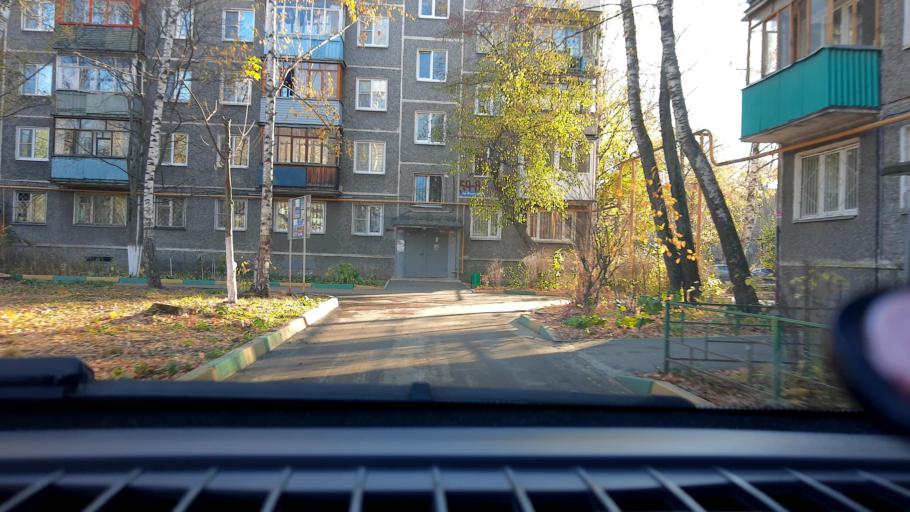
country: RU
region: Nizjnij Novgorod
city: Nizhniy Novgorod
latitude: 56.2759
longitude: 43.9144
